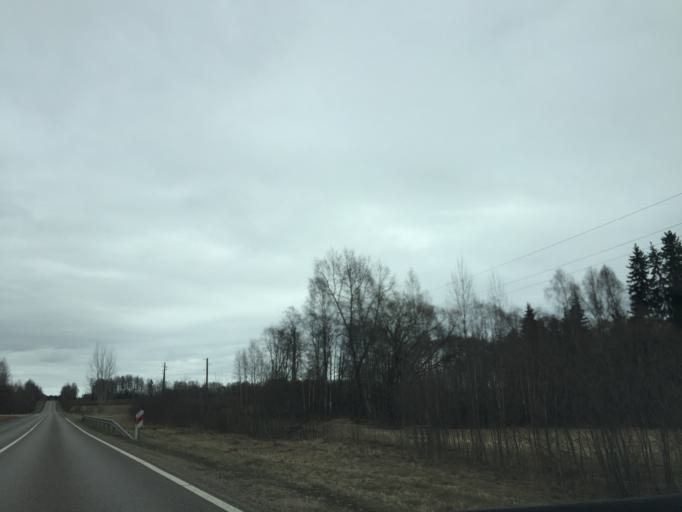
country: LV
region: Kraslavas Rajons
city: Kraslava
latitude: 55.9112
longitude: 27.0725
